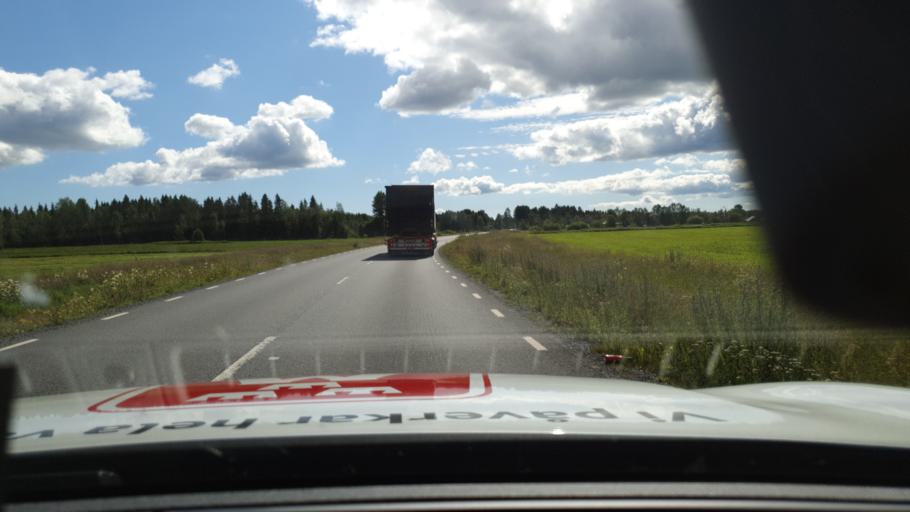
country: SE
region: Norrbotten
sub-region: Lulea Kommun
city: Gammelstad
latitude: 65.7964
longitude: 22.0670
